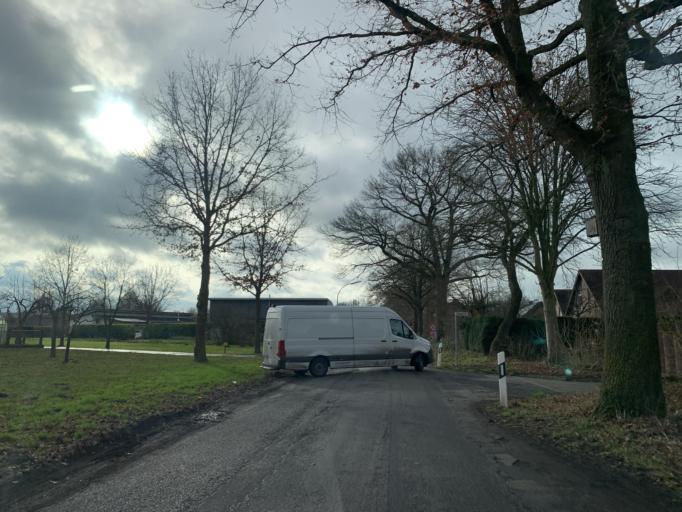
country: DE
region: North Rhine-Westphalia
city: Ludinghausen
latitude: 51.7770
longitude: 7.4642
